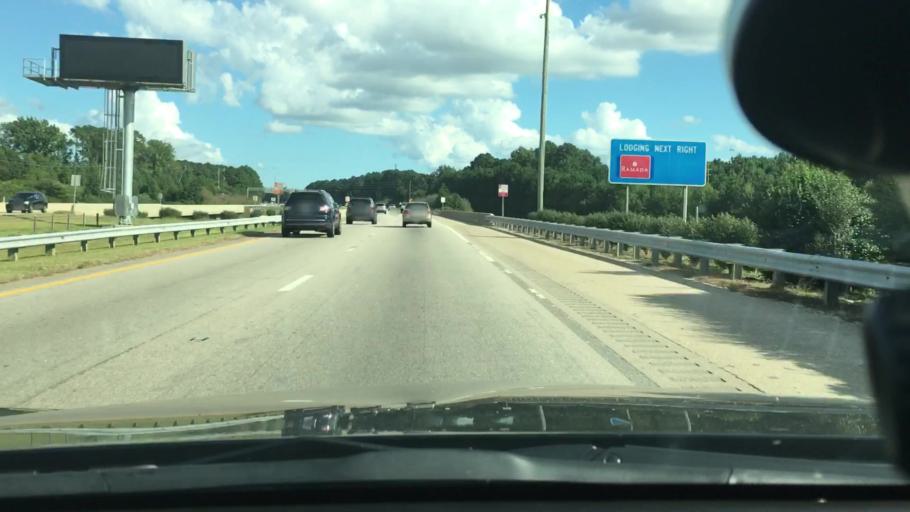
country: US
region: North Carolina
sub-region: Wake County
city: Cary
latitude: 35.8078
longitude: -78.7241
